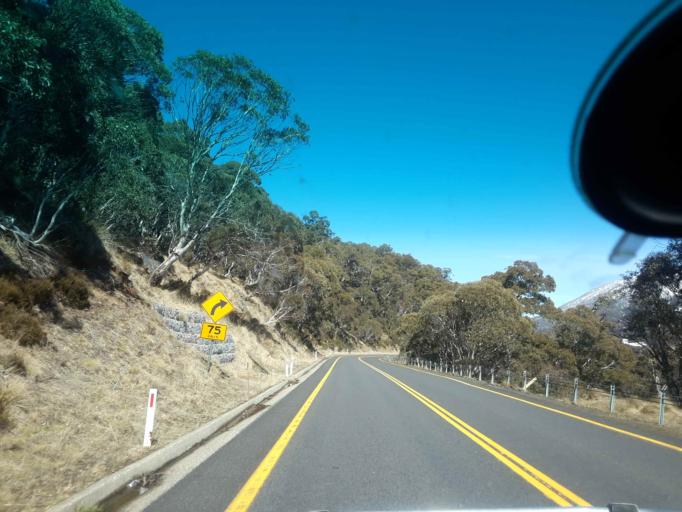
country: AU
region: New South Wales
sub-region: Snowy River
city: Jindabyne
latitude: -36.4942
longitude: 148.3280
